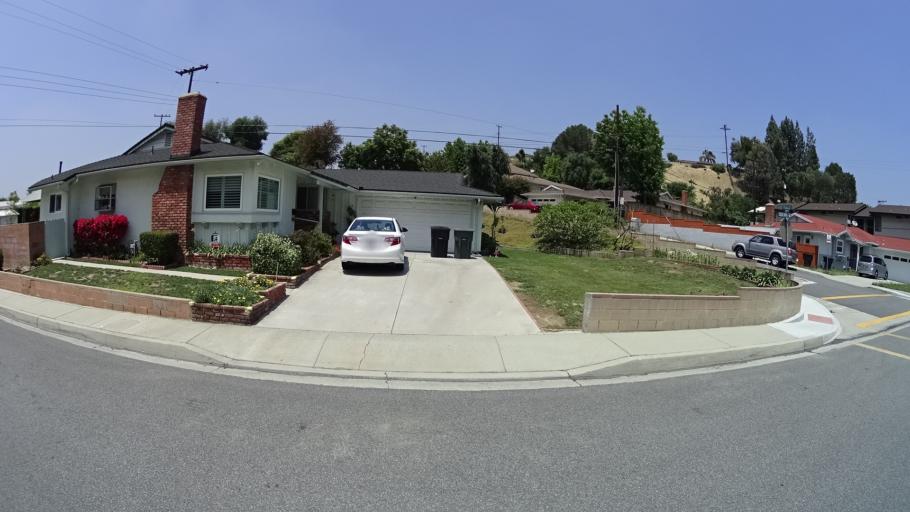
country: US
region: California
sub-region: Los Angeles County
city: Belvedere
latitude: 34.0592
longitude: -118.1542
